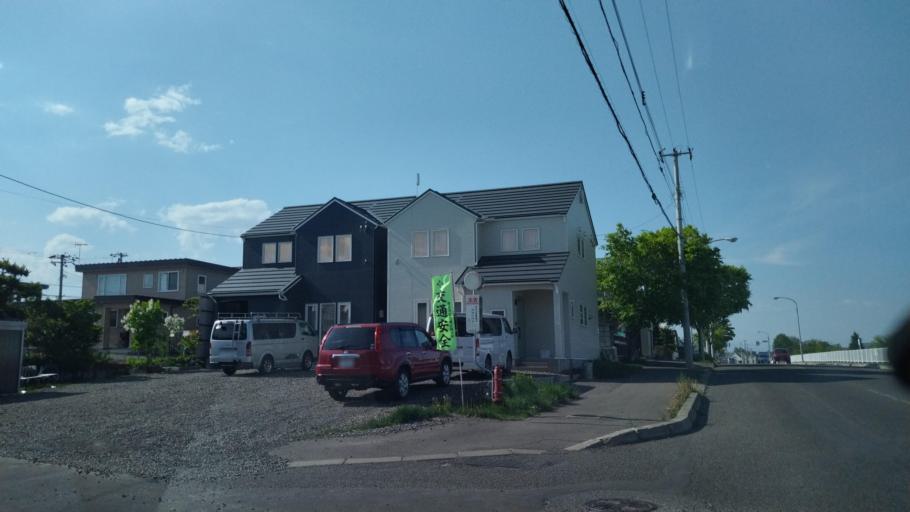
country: JP
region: Hokkaido
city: Obihiro
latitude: 42.9194
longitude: 143.1578
